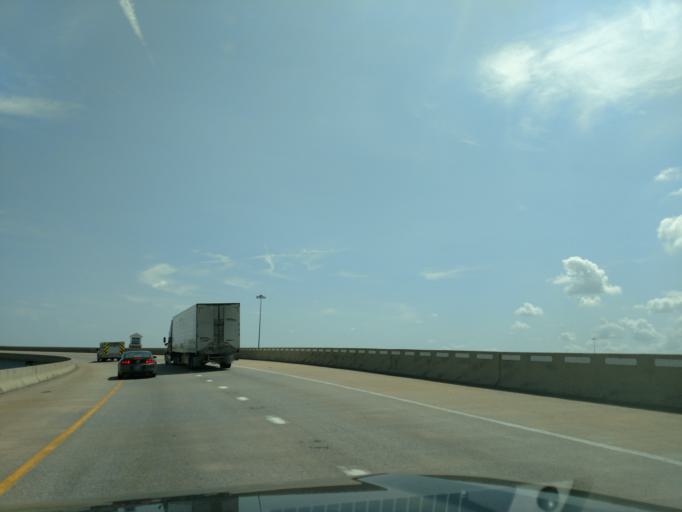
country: US
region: Mississippi
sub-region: Rankin County
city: Pearl
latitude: 32.2709
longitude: -90.1570
